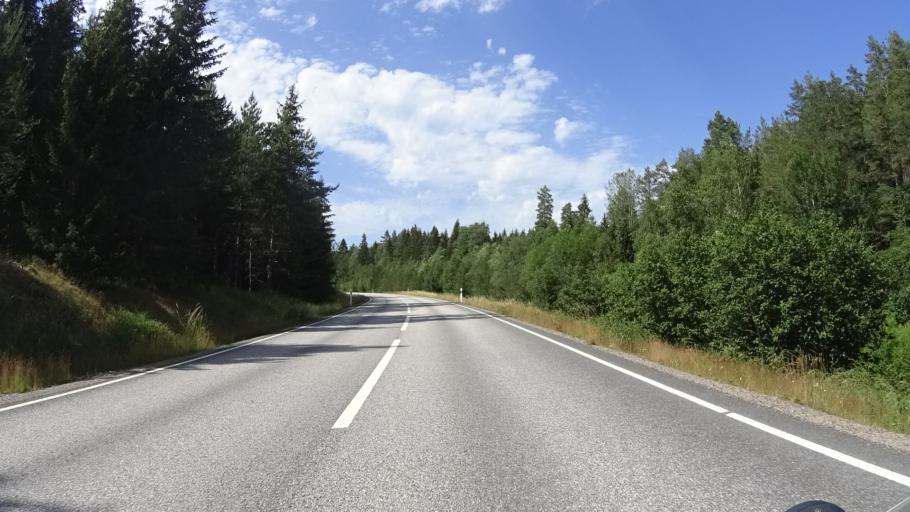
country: SE
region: Kalmar
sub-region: Vasterviks Kommun
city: Overum
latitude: 58.0705
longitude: 16.1997
